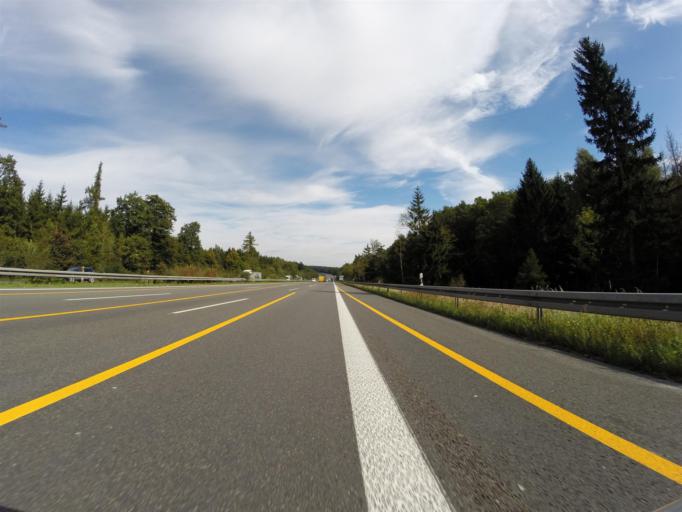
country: DE
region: Saxony
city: Nossen
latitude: 51.0209
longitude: 13.2566
